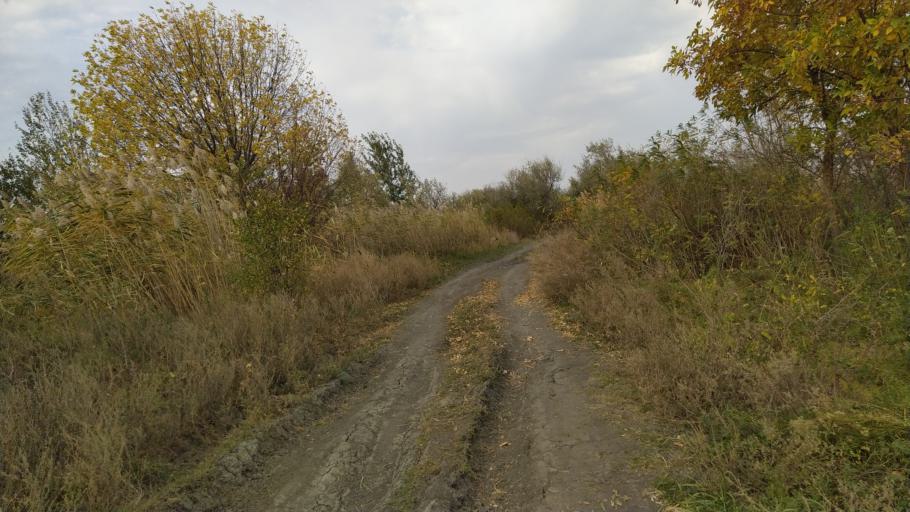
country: RU
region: Rostov
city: Kuleshovka
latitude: 47.1459
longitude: 39.5861
